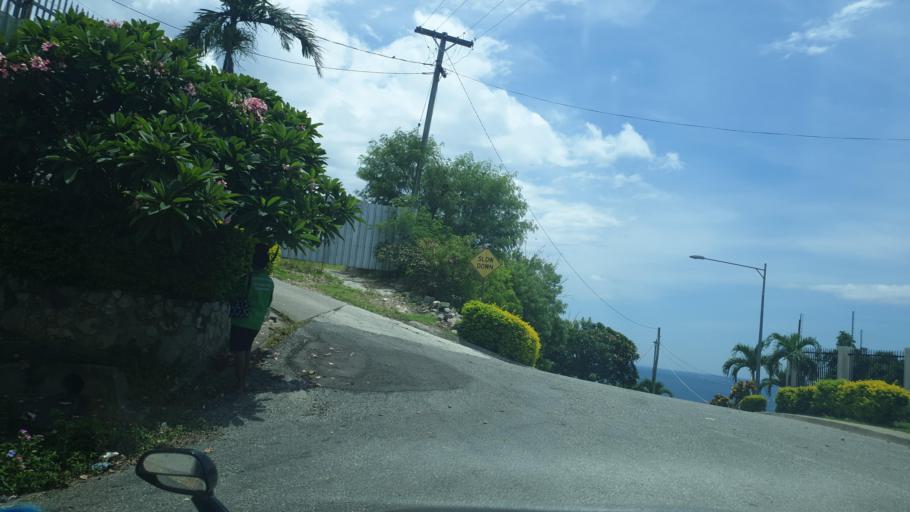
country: PG
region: National Capital
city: Port Moresby
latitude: -9.4758
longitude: 147.1555
